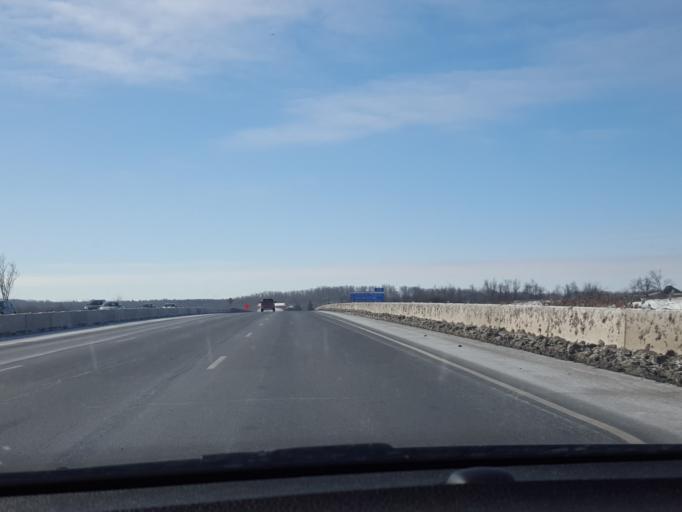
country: CA
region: Ontario
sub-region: Halton
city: Milton
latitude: 43.5018
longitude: -79.9585
